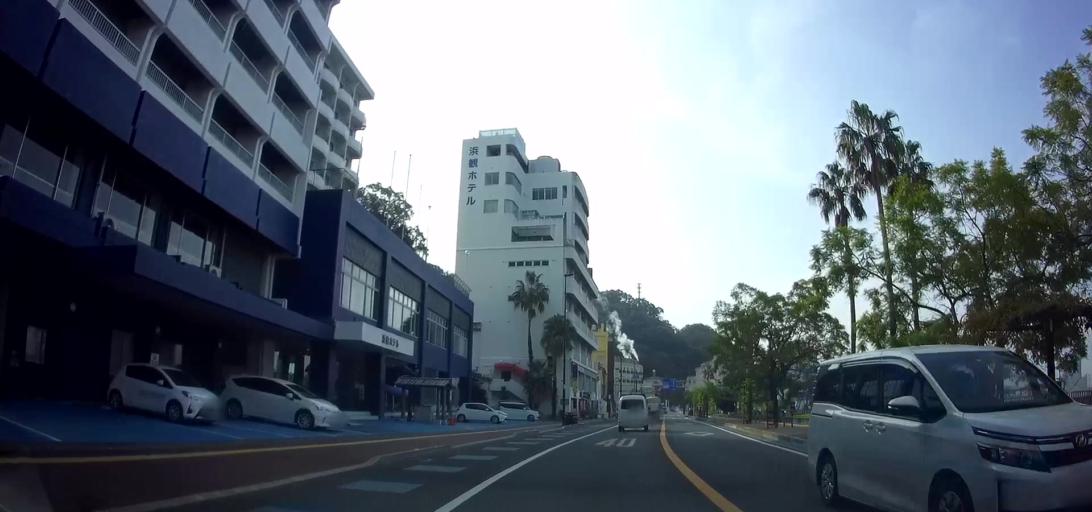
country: JP
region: Nagasaki
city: Shimabara
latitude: 32.7284
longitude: 130.2068
